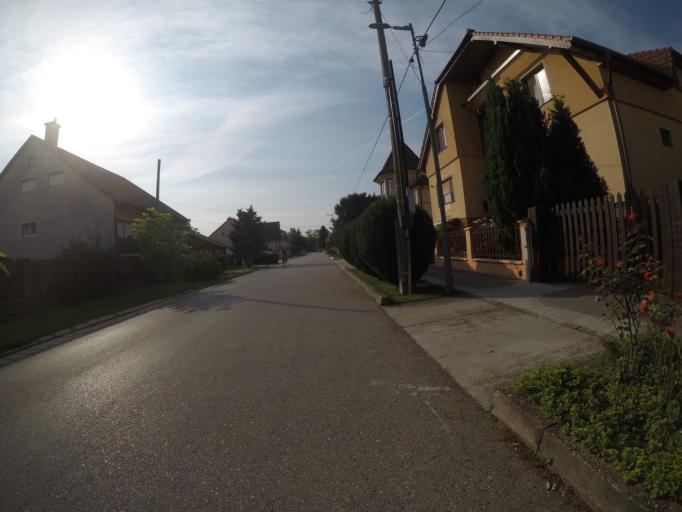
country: SK
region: Trnavsky
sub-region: Okres Dunajska Streda
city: Velky Meder
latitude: 47.8520
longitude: 17.7624
